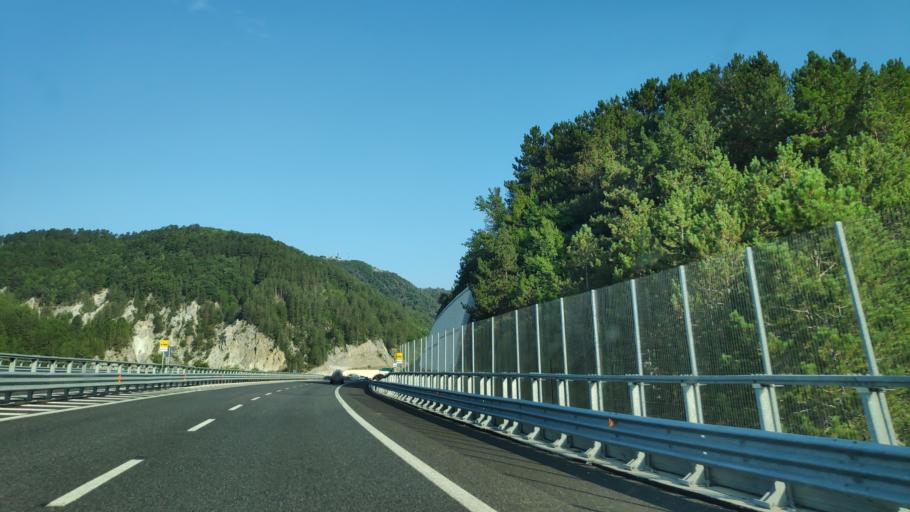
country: IT
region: Calabria
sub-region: Provincia di Cosenza
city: Mormanno
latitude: 39.8776
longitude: 15.9917
